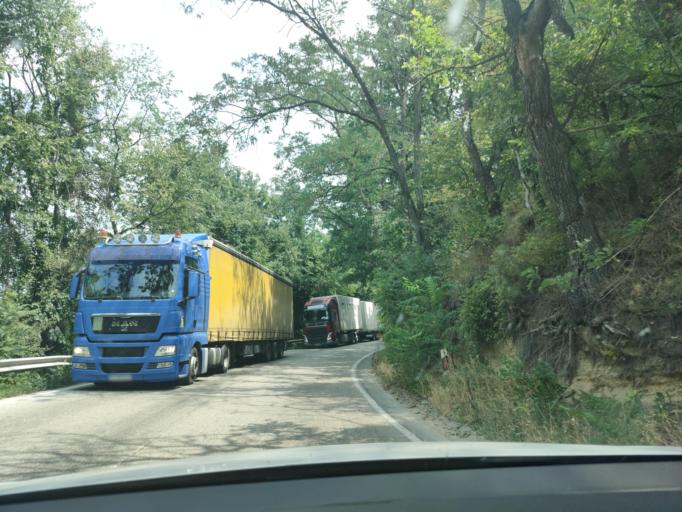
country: BG
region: Vidin
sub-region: Obshtina Dimovo
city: Dimovo
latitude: 43.7356
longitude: 22.7268
